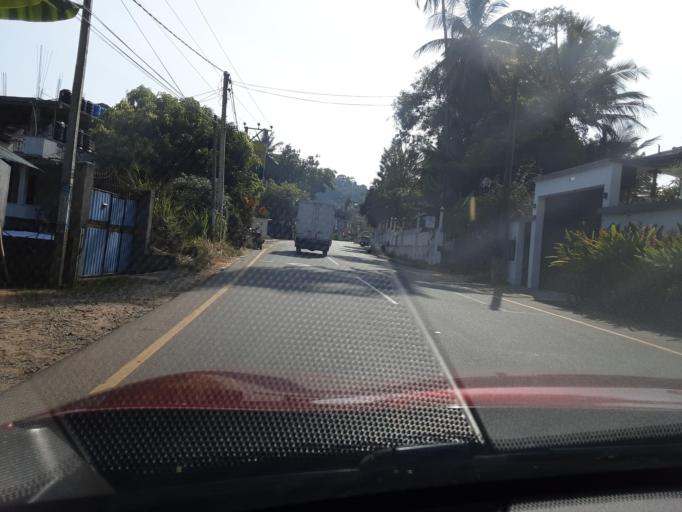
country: LK
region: Uva
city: Badulla
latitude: 6.9844
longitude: 81.0680
